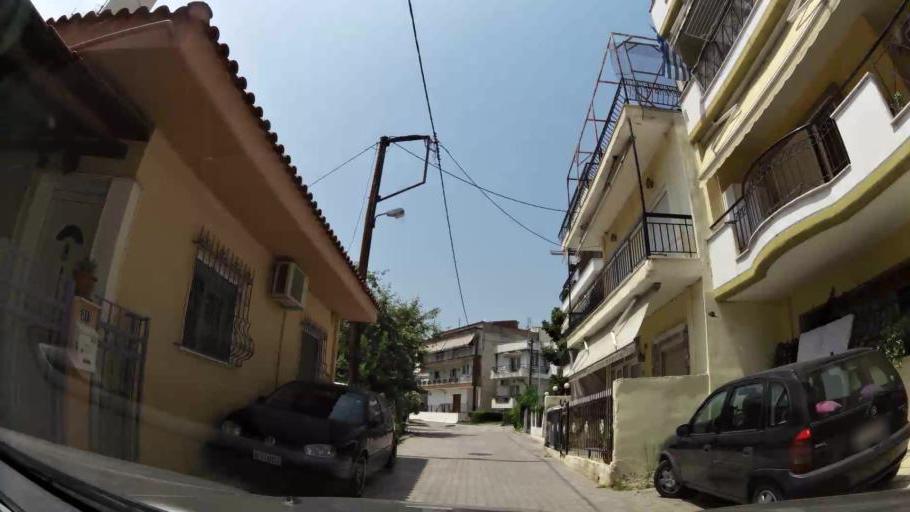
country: GR
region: Central Macedonia
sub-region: Nomos Thessalonikis
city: Evosmos
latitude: 40.6642
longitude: 22.9100
